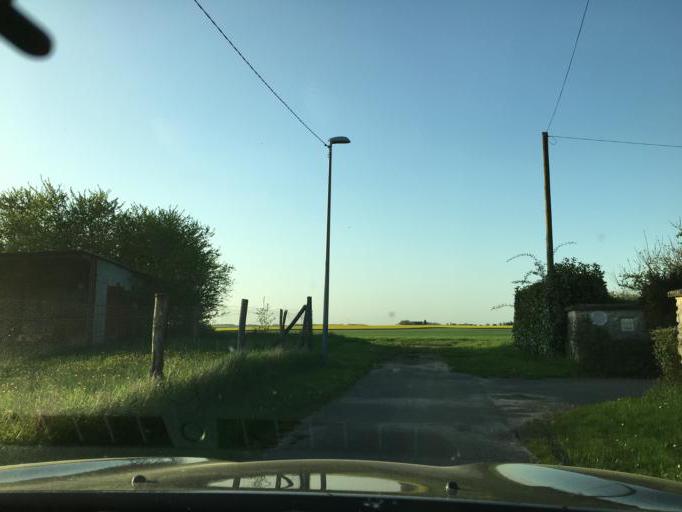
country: FR
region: Centre
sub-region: Departement du Loiret
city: Tavers
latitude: 47.8082
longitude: 1.5286
